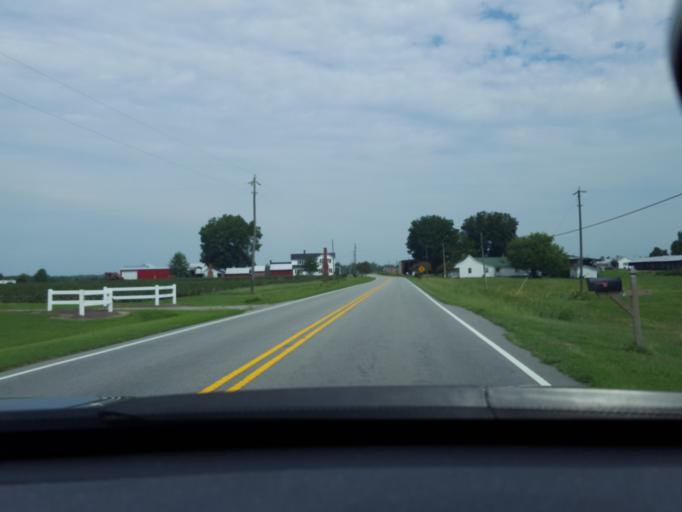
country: US
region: North Carolina
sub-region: Chowan County
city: Edenton
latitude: 36.1886
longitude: -76.6612
